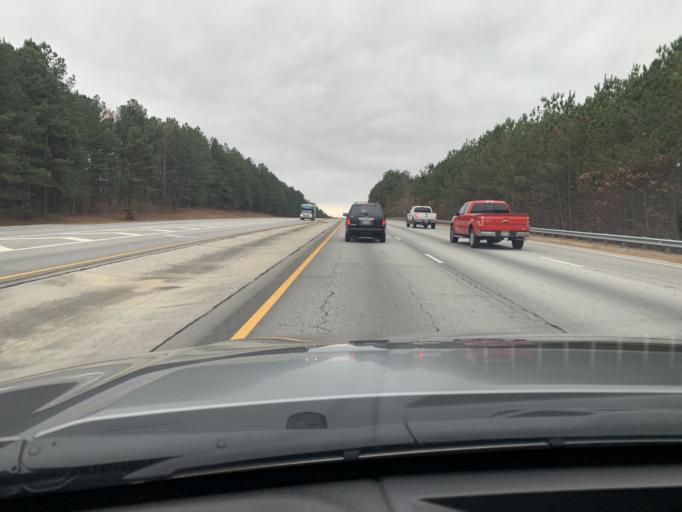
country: US
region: Georgia
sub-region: Habersham County
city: Demorest
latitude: 34.5596
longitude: -83.5245
